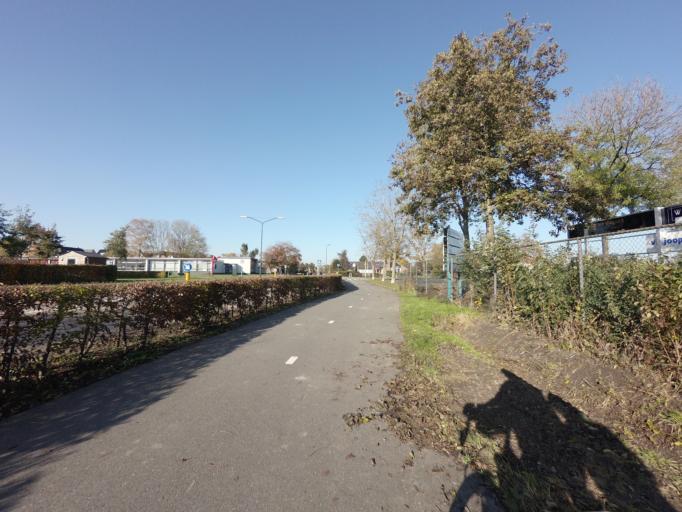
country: NL
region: North Brabant
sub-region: Gemeente Waalwijk
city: Waalwijk
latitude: 51.7289
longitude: 5.0549
